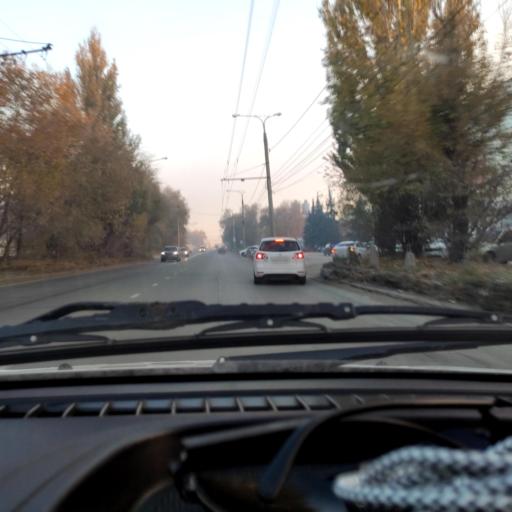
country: RU
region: Samara
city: Tol'yatti
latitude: 53.5655
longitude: 49.4567
